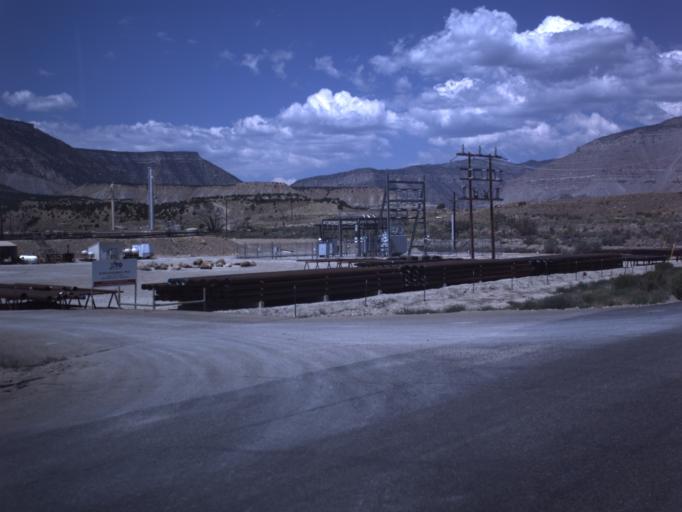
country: US
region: Utah
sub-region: Emery County
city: Orangeville
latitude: 39.2436
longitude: -111.0910
